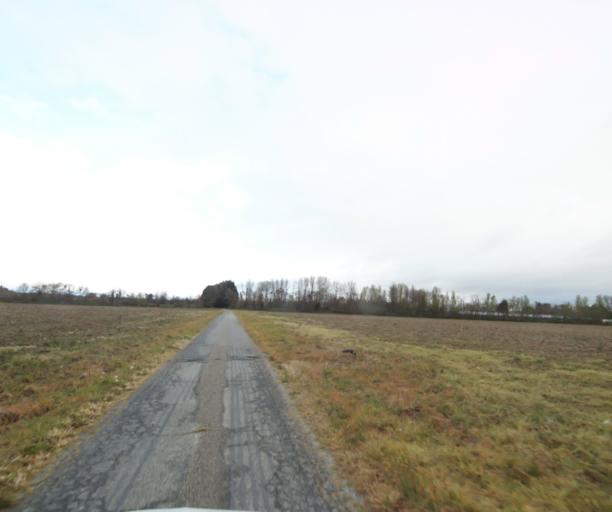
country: FR
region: Midi-Pyrenees
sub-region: Departement de l'Ariege
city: Saverdun
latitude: 43.2244
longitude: 1.5978
